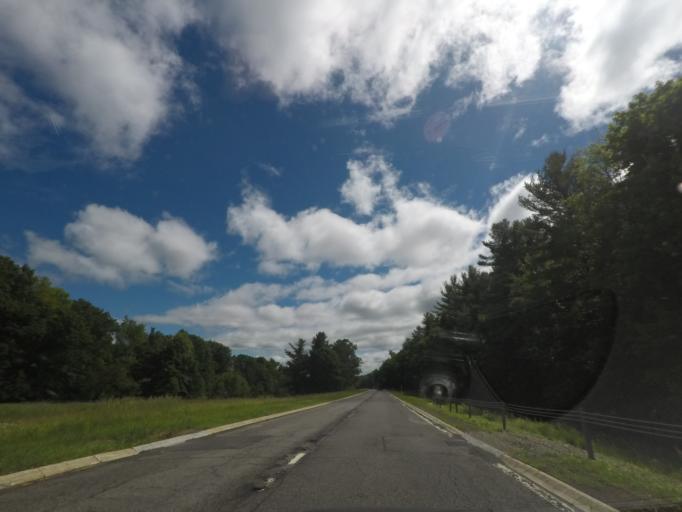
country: US
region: New York
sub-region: Columbia County
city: Chatham
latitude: 42.3063
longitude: -73.5805
